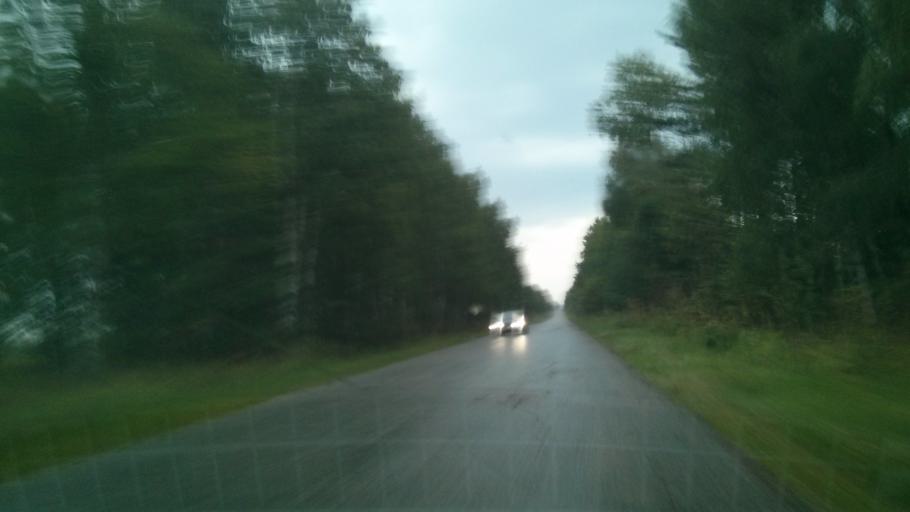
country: RU
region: Nizjnij Novgorod
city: Shimorskoye
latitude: 55.3393
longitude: 41.8764
